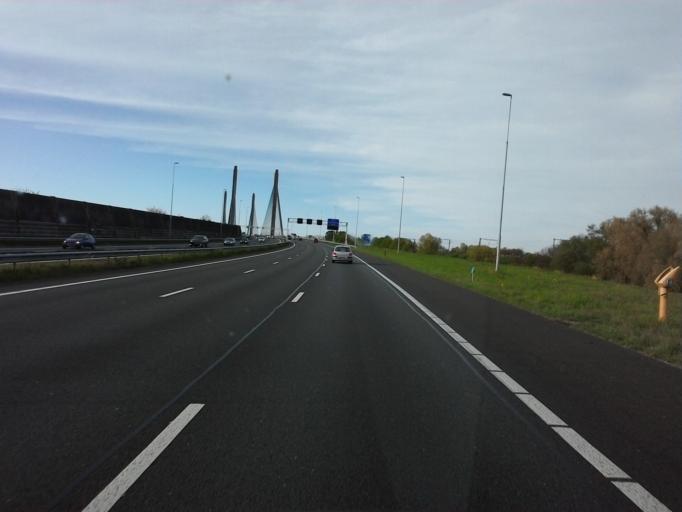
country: NL
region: Gelderland
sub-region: Gemeente Zaltbommel
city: Zaltbommel
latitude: 51.8125
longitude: 5.2606
